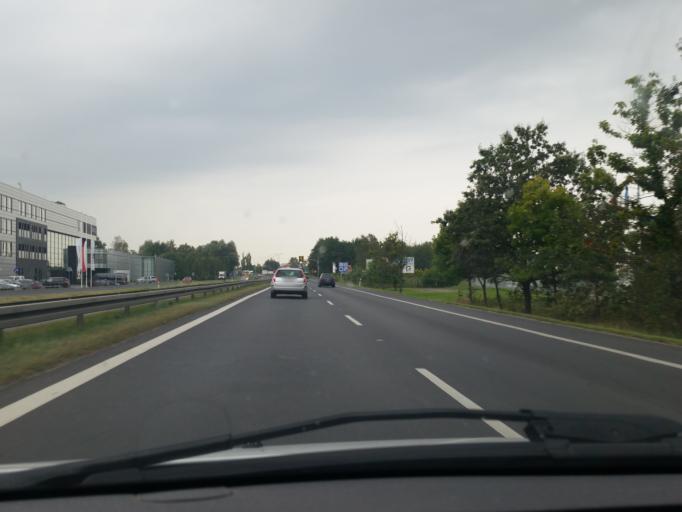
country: PL
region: Masovian Voivodeship
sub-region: Powiat pruszkowski
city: Nadarzyn
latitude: 52.0838
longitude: 20.7992
